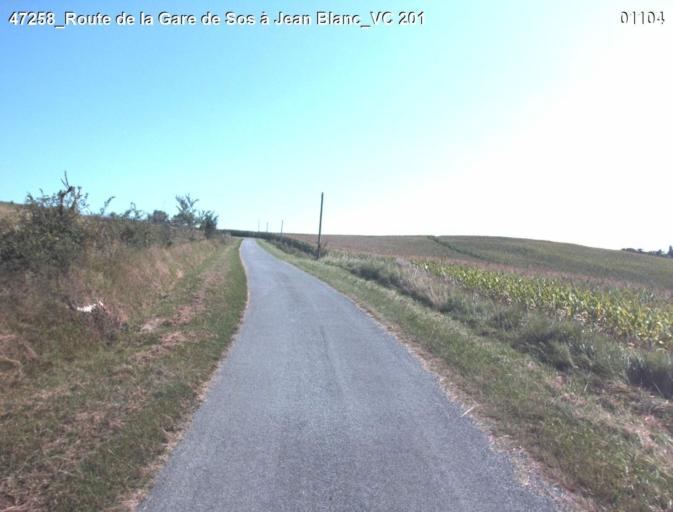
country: FR
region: Midi-Pyrenees
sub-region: Departement du Gers
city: Montreal
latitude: 44.0340
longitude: 0.1494
